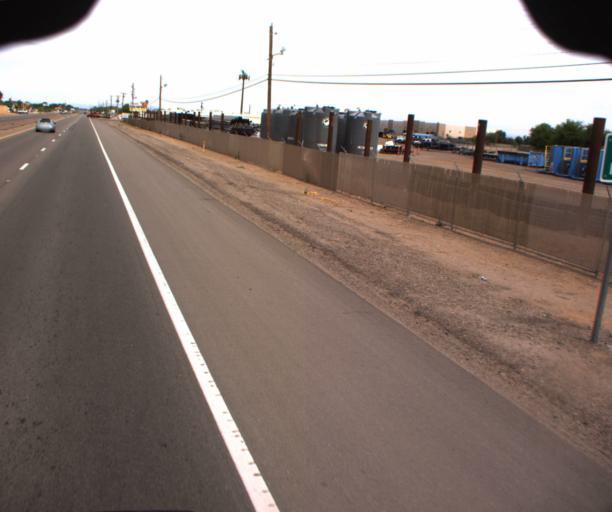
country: US
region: Arizona
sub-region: Maricopa County
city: Sun Lakes
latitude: 33.2089
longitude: -111.8411
